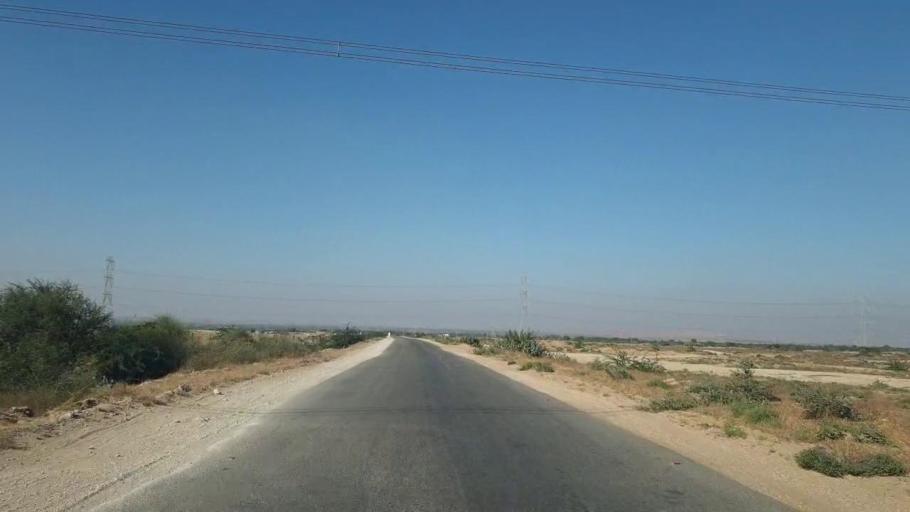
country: PK
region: Sindh
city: Gharo
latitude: 25.1756
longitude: 67.6597
